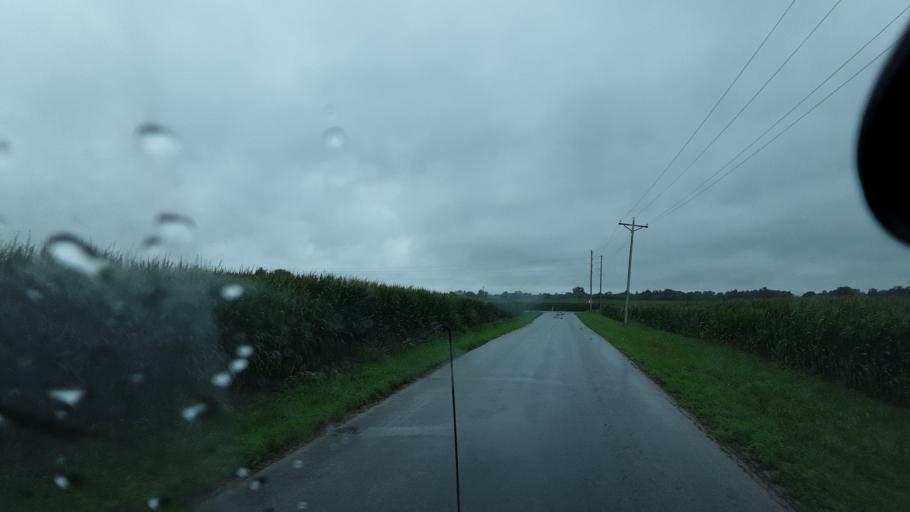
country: US
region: Indiana
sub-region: Adams County
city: Decatur
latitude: 40.7594
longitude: -84.8576
